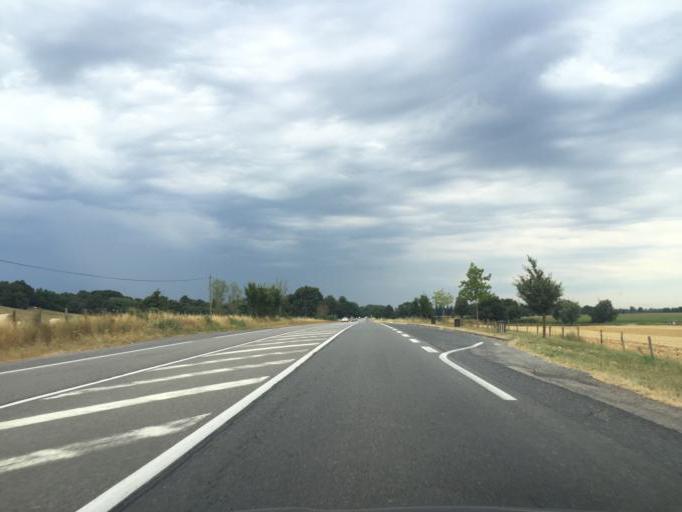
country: FR
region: Auvergne
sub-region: Departement de l'Allier
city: Bessay-sur-Allier
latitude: 46.4739
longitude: 3.3675
